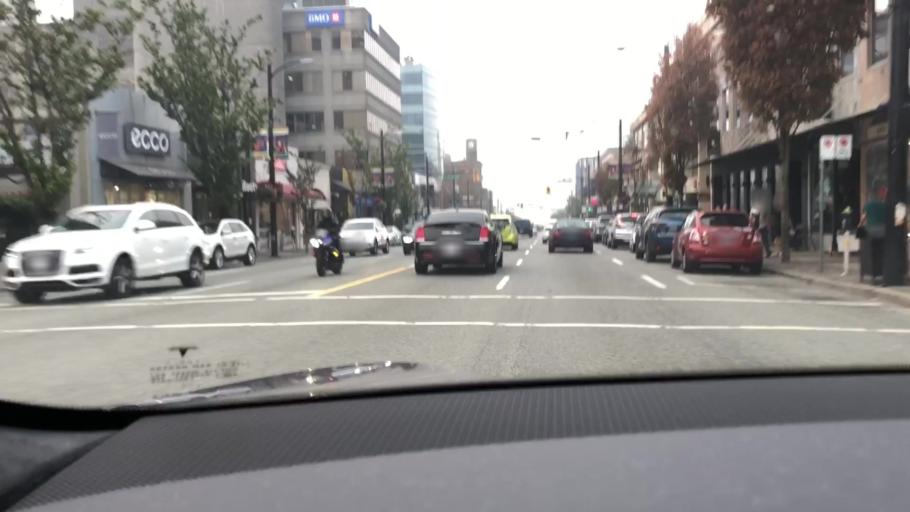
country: CA
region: British Columbia
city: West End
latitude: 49.2617
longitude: -123.1386
